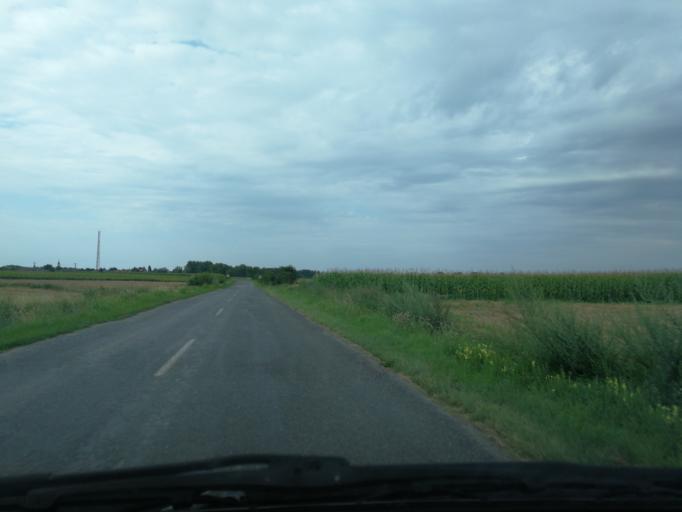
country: HU
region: Bacs-Kiskun
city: Kalocsa
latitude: 46.4582
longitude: 19.0346
